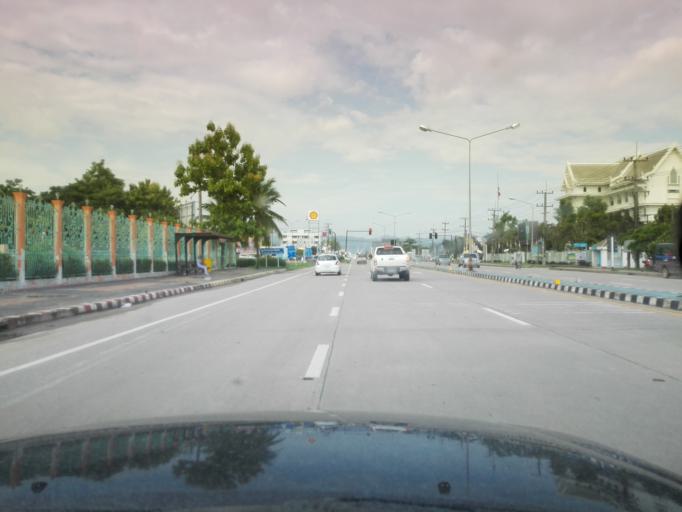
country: TH
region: Tak
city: Mae Sot
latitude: 16.7219
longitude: 98.5677
